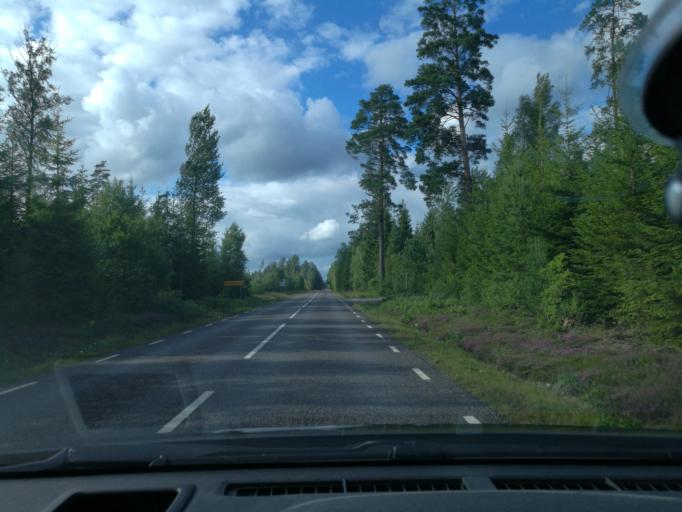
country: SE
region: Kronoberg
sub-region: Vaxjo Kommun
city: Braas
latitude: 57.0690
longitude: 15.0087
